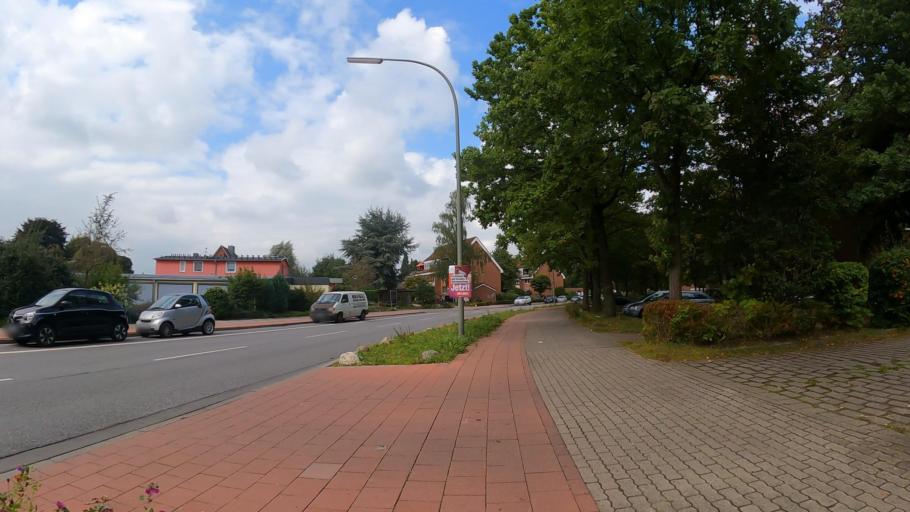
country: DE
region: Schleswig-Holstein
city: Elmshorn
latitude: 53.7362
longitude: 9.6702
